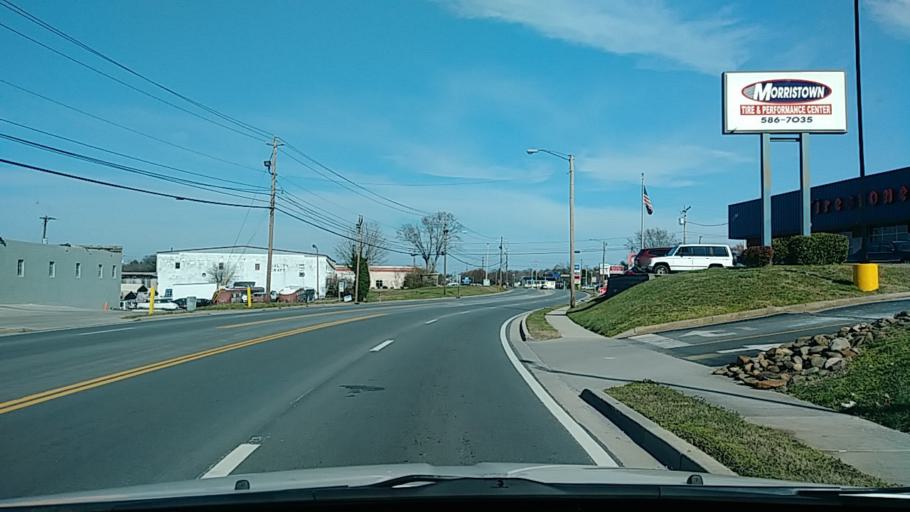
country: US
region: Tennessee
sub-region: Hamblen County
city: Morristown
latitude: 36.2152
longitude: -83.2852
